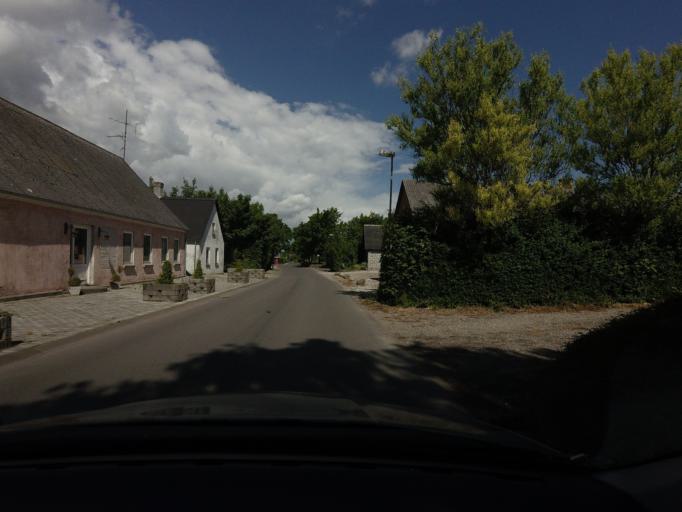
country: DK
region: Central Jutland
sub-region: Norddjurs Kommune
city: Grenaa
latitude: 56.4730
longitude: 10.8635
